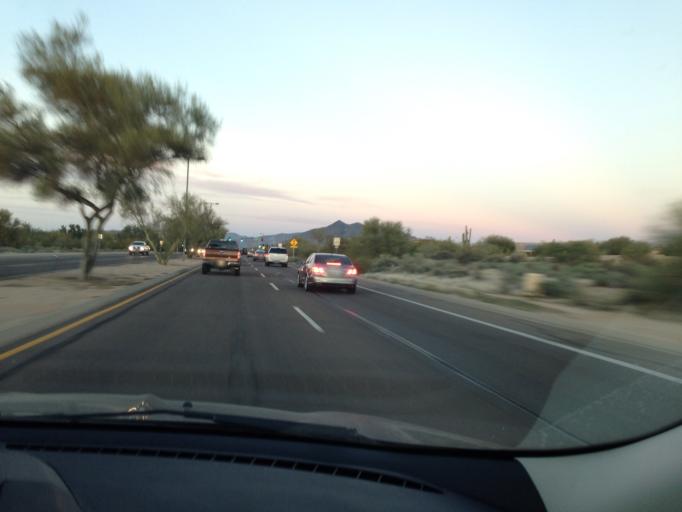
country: US
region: Arizona
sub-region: Maricopa County
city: Cave Creek
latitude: 33.7681
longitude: -111.9830
